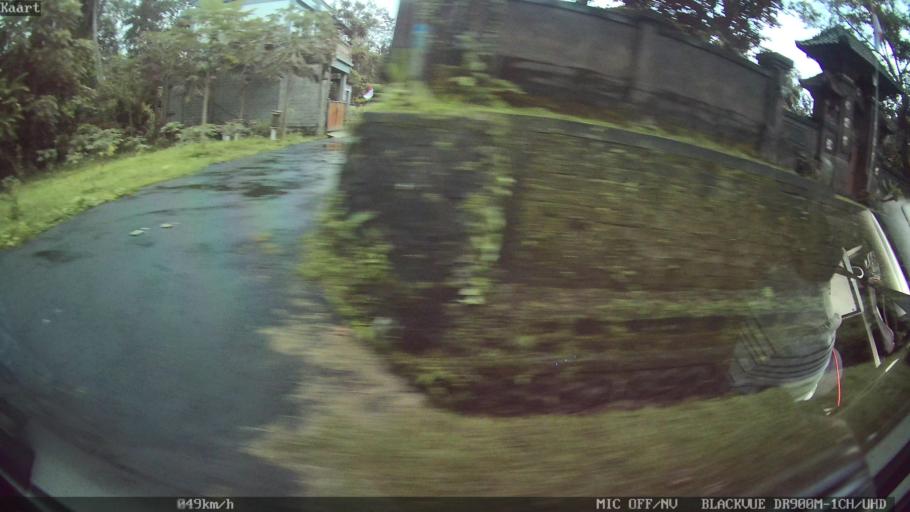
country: ID
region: Bali
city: Pegongan
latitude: -8.4913
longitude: 115.2376
